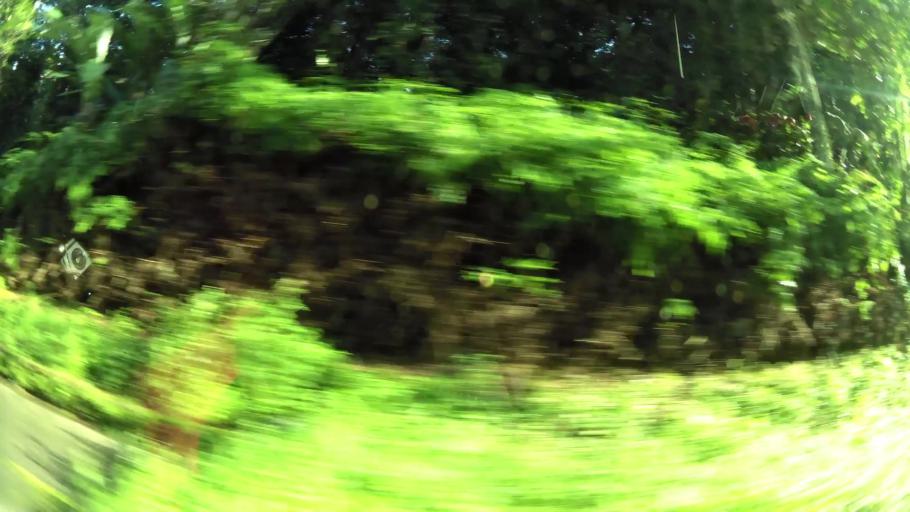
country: GP
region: Guadeloupe
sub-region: Guadeloupe
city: Bouillante
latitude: 16.1785
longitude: -61.6897
